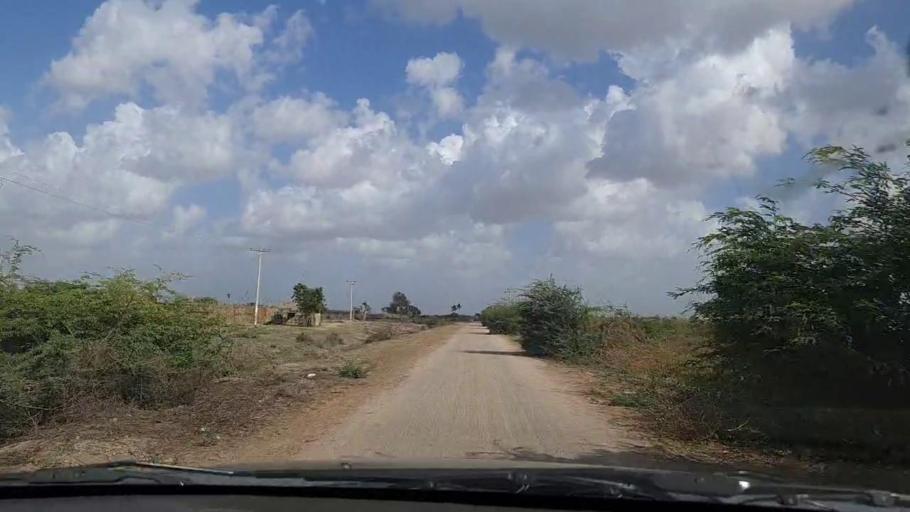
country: PK
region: Sindh
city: Keti Bandar
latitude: 24.0967
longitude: 67.6068
